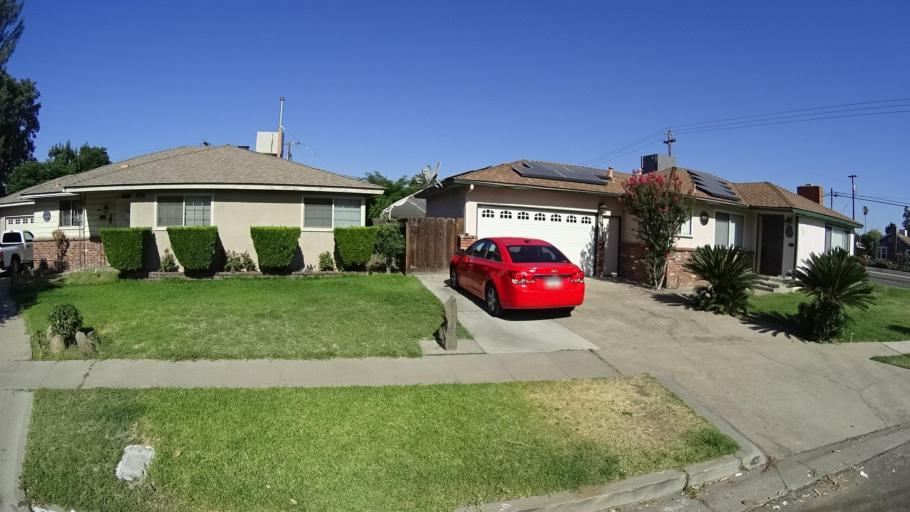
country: US
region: California
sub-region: Fresno County
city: Fresno
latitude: 36.7865
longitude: -119.7609
